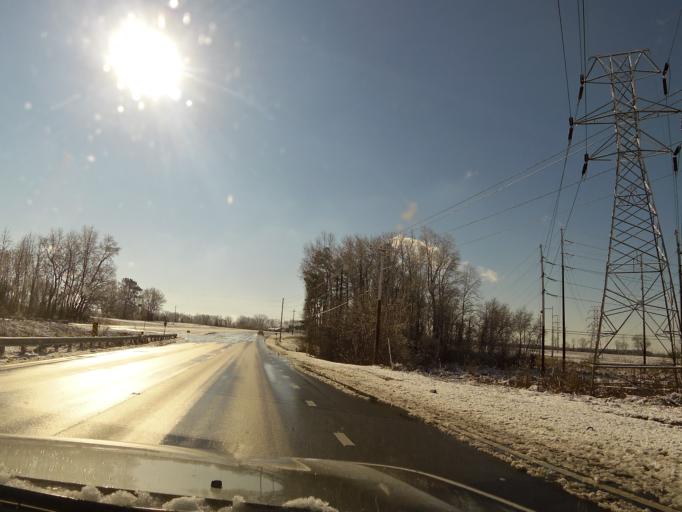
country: US
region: North Carolina
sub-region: Wilson County
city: Elm City
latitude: 35.7814
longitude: -77.8585
